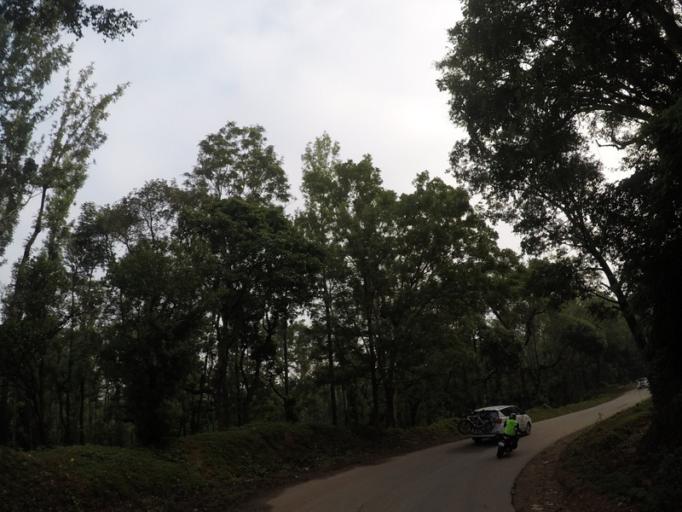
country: IN
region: Karnataka
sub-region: Chikmagalur
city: Chikmagalur
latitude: 13.4596
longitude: 75.7978
